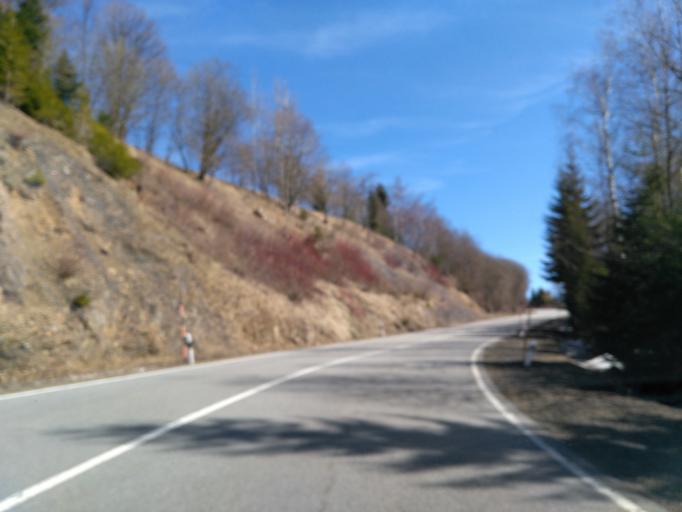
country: DE
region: Saxony
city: Kurort Oberwiesenthal
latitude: 50.4153
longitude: 12.9558
